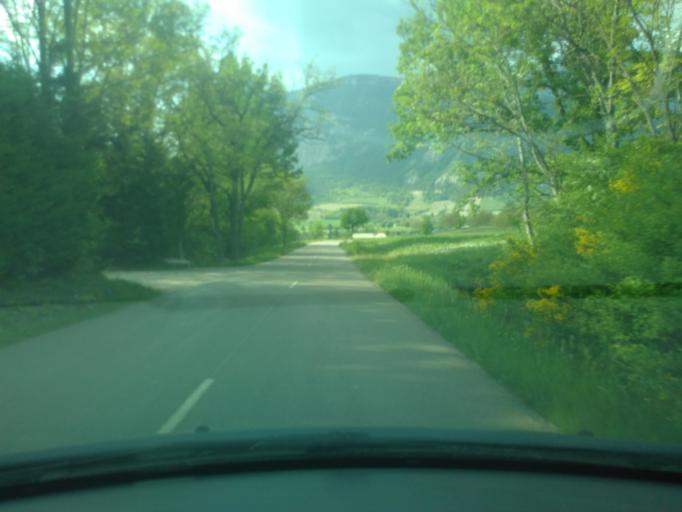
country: FR
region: Rhone-Alpes
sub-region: Departement de la Drome
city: Die
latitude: 44.6808
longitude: 5.4698
